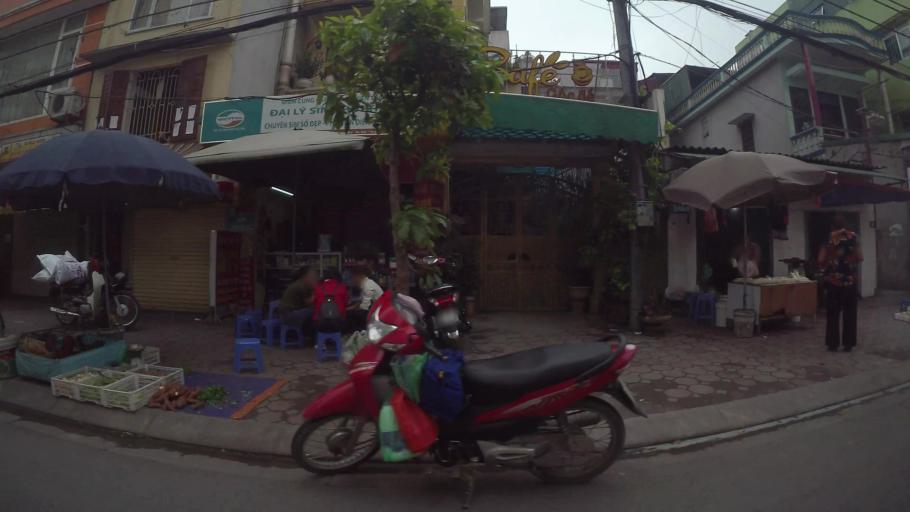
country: VN
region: Ha Noi
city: Hai BaTrung
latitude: 20.9940
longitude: 105.8564
